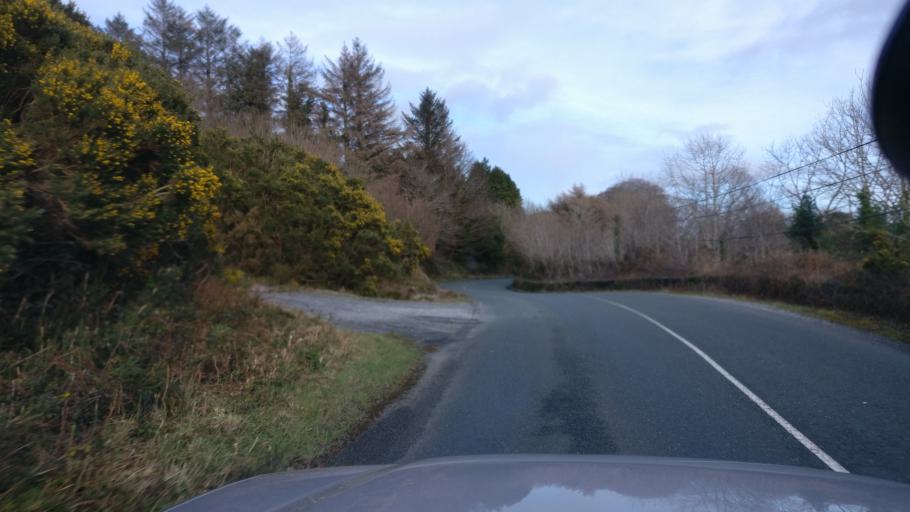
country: IE
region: Connaught
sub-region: County Galway
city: Oughterard
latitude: 53.5171
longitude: -9.4027
